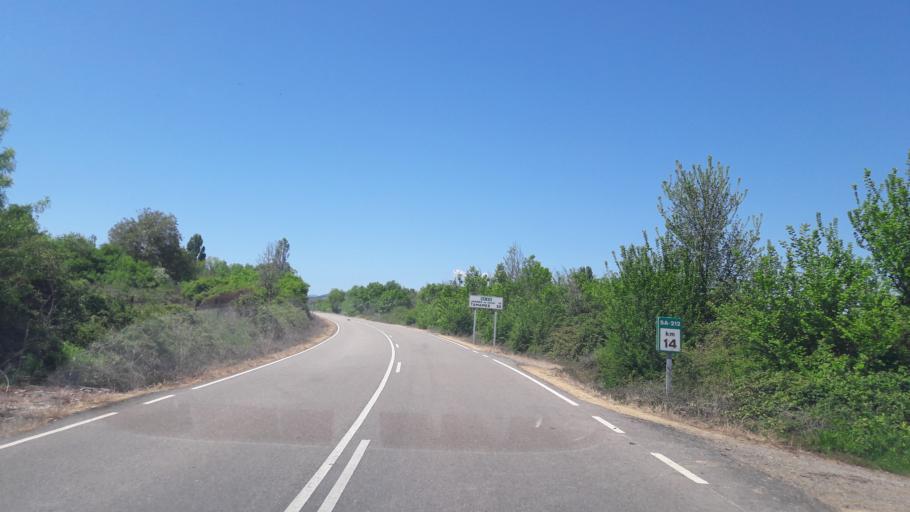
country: ES
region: Castille and Leon
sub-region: Provincia de Salamanca
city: Endrinal
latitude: 40.5912
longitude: -5.8082
